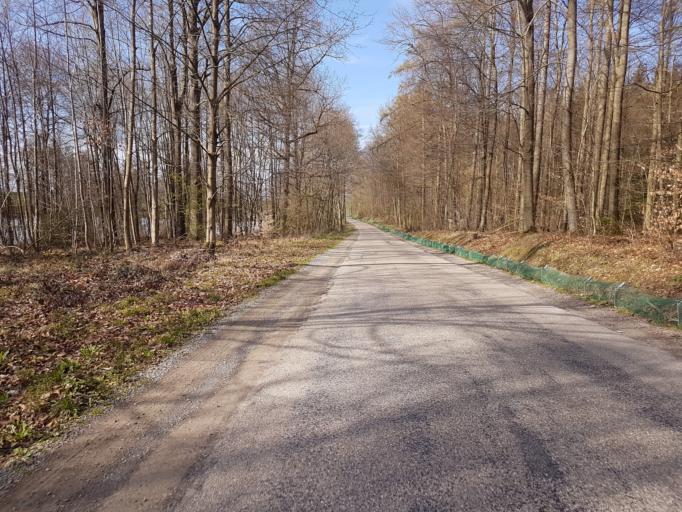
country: DE
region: Baden-Wuerttemberg
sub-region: Regierungsbezirk Stuttgart
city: Forchtenberg
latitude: 49.3249
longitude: 9.5484
